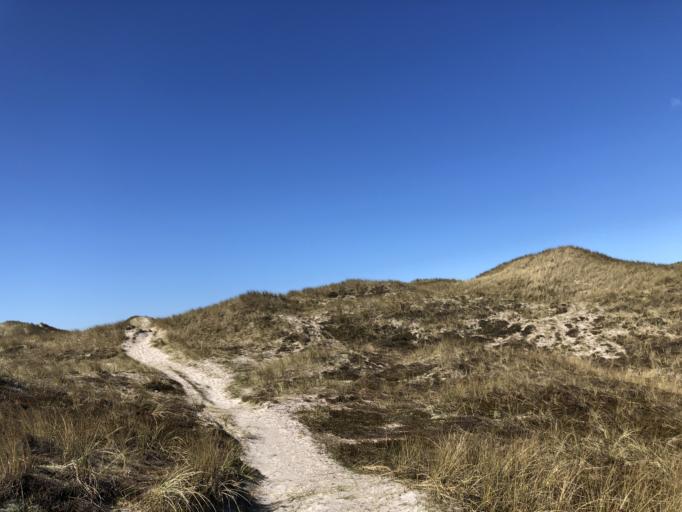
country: DK
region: Central Jutland
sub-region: Holstebro Kommune
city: Ulfborg
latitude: 56.3054
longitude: 8.1257
